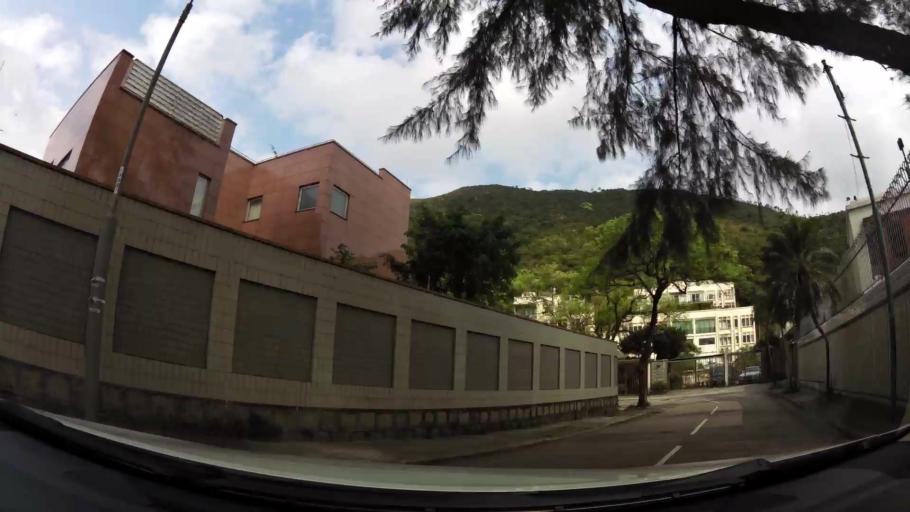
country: HK
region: Wanchai
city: Wan Chai
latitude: 22.2673
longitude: 114.1929
